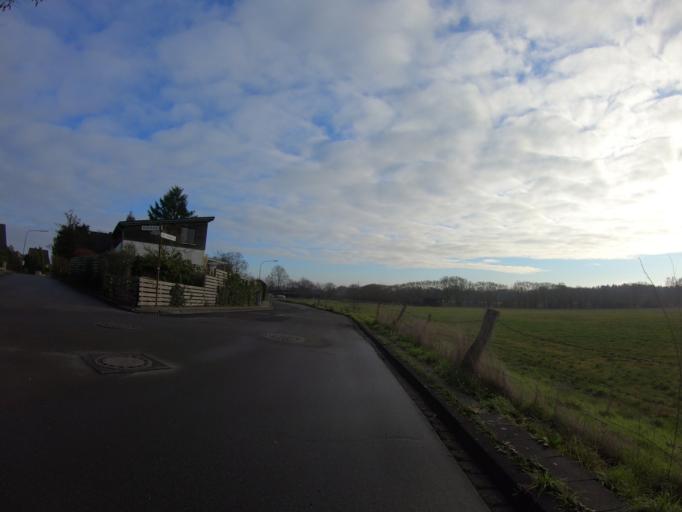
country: DE
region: Lower Saxony
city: Gifhorn
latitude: 52.4812
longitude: 10.5186
